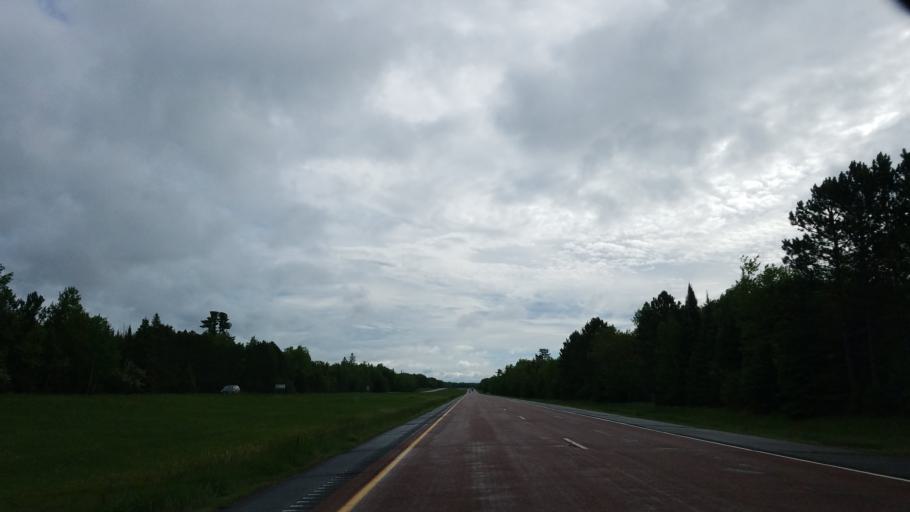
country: US
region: Minnesota
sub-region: Saint Louis County
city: Arnold
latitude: 46.9144
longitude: -91.8774
